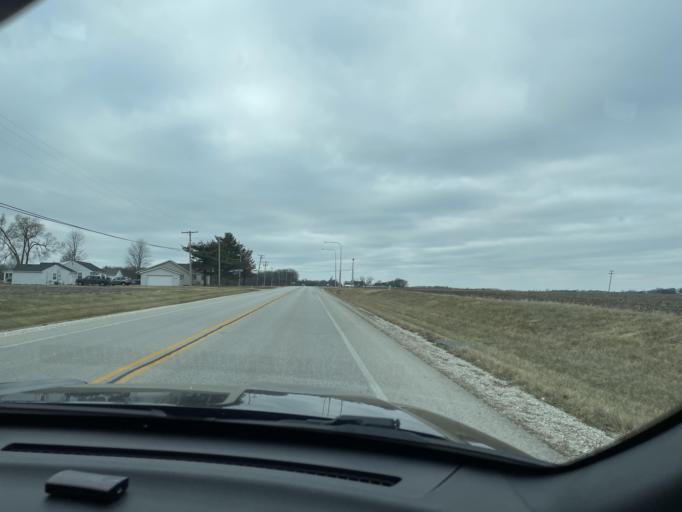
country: US
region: Illinois
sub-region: Sangamon County
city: Leland Grove
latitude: 39.8196
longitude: -89.7188
